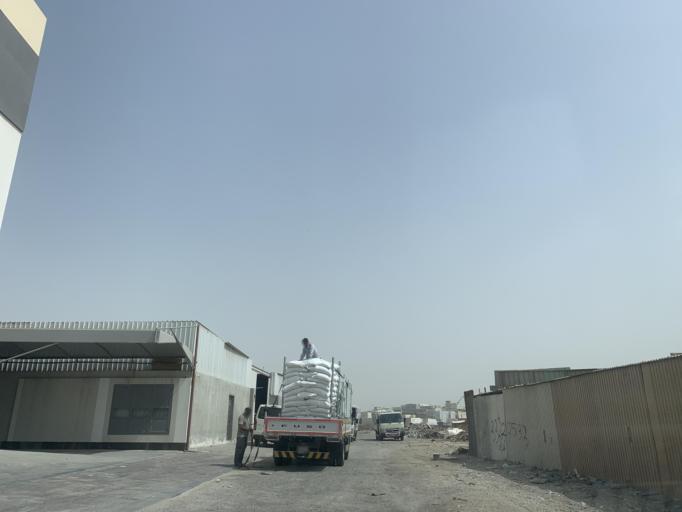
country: BH
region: Northern
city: Madinat `Isa
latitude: 26.1873
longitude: 50.5215
